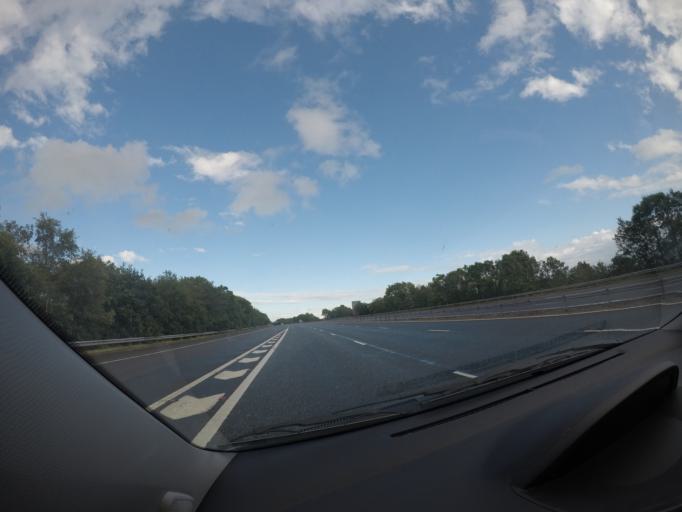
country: GB
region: Scotland
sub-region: Dumfries and Galloway
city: Annan
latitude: 55.0503
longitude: -3.2143
